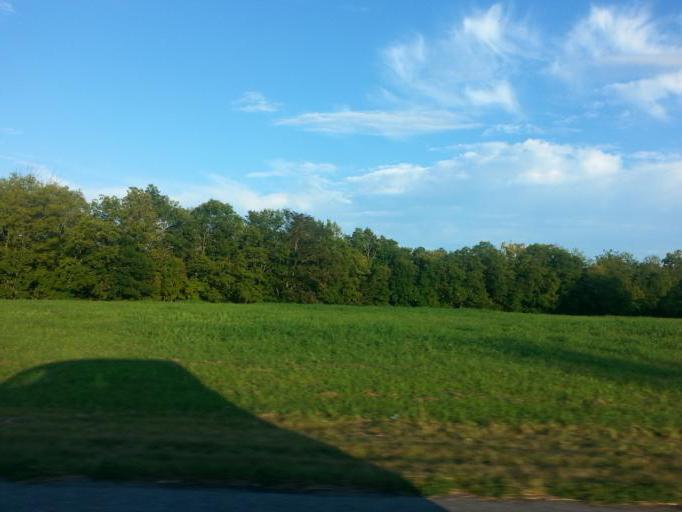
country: US
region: Tennessee
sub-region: Knox County
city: Mascot
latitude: 36.1113
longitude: -83.7350
